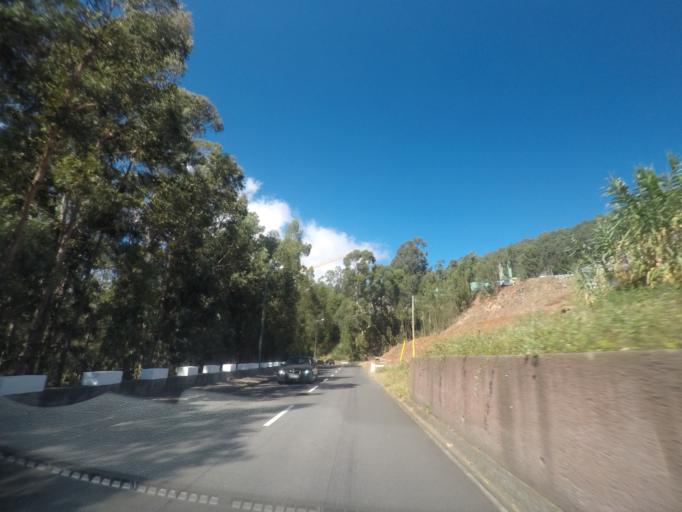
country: PT
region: Madeira
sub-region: Ribeira Brava
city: Campanario
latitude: 32.6837
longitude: -17.0409
